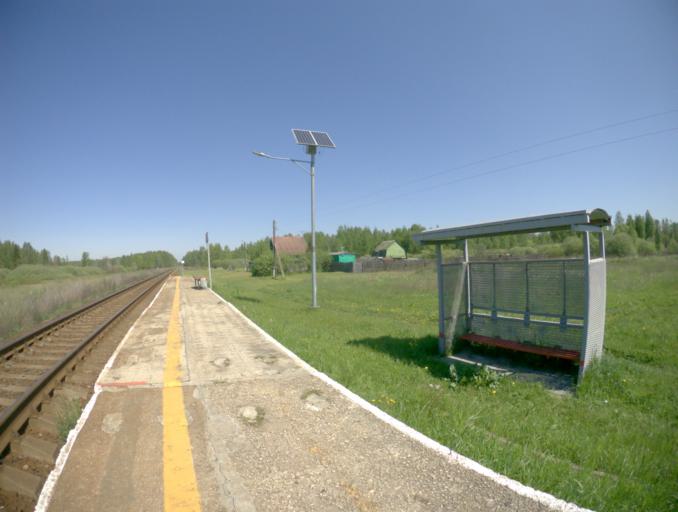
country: RU
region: Vladimir
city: Anopino
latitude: 55.6822
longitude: 40.6327
